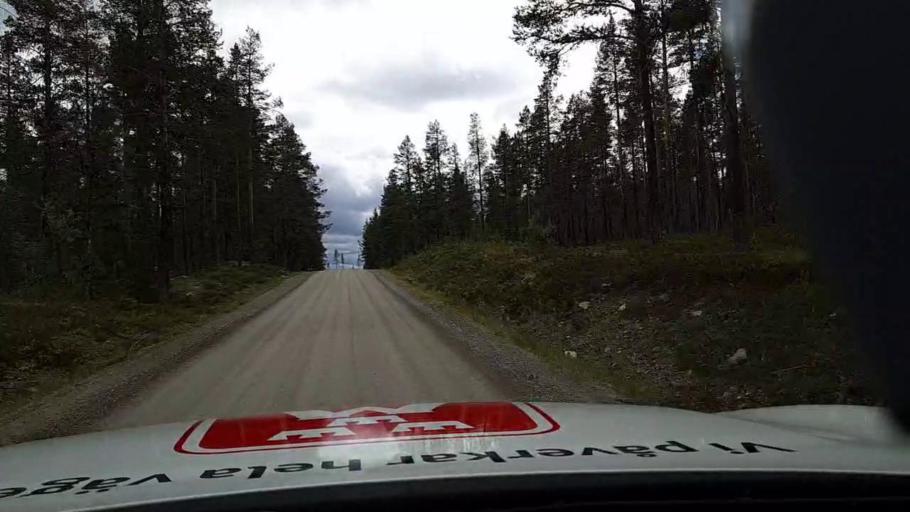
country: SE
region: Jaemtland
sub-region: Are Kommun
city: Jarpen
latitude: 62.8167
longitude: 13.8093
